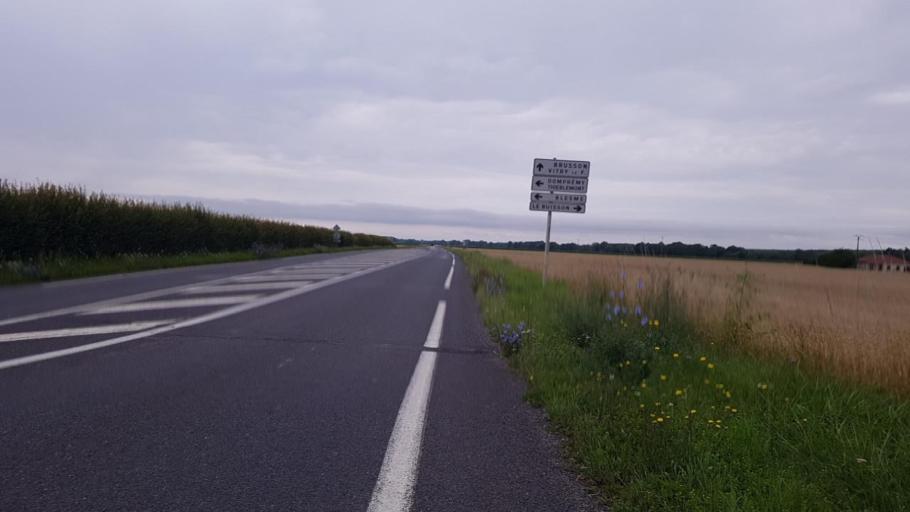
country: FR
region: Champagne-Ardenne
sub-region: Departement de la Marne
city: Pargny-sur-Saulx
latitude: 48.7585
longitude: 4.7537
